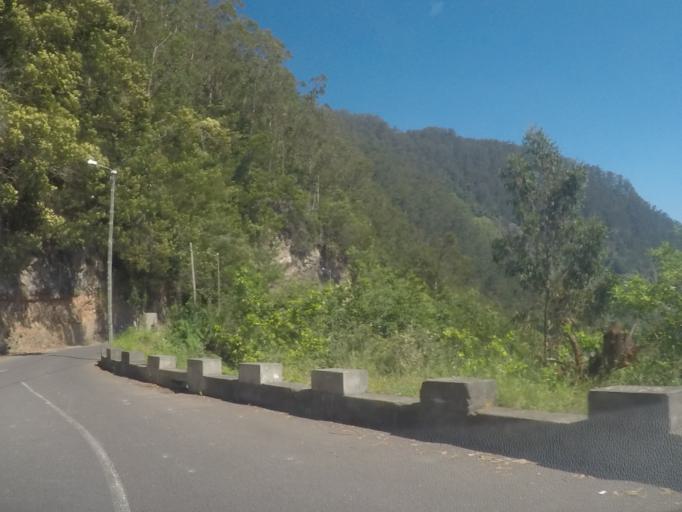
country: PT
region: Madeira
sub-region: Camara de Lobos
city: Curral das Freiras
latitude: 32.6860
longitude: -16.9694
